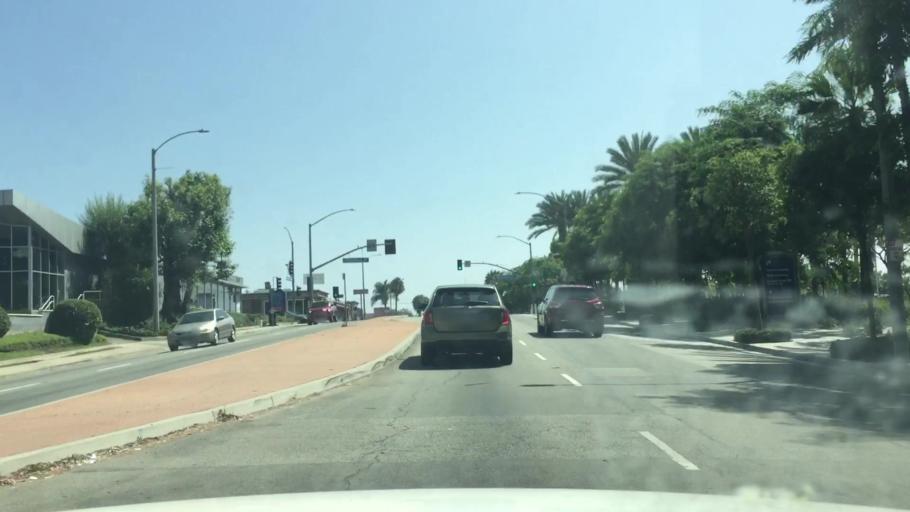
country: US
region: California
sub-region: Los Angeles County
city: Signal Hill
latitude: 33.8080
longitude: -118.1851
